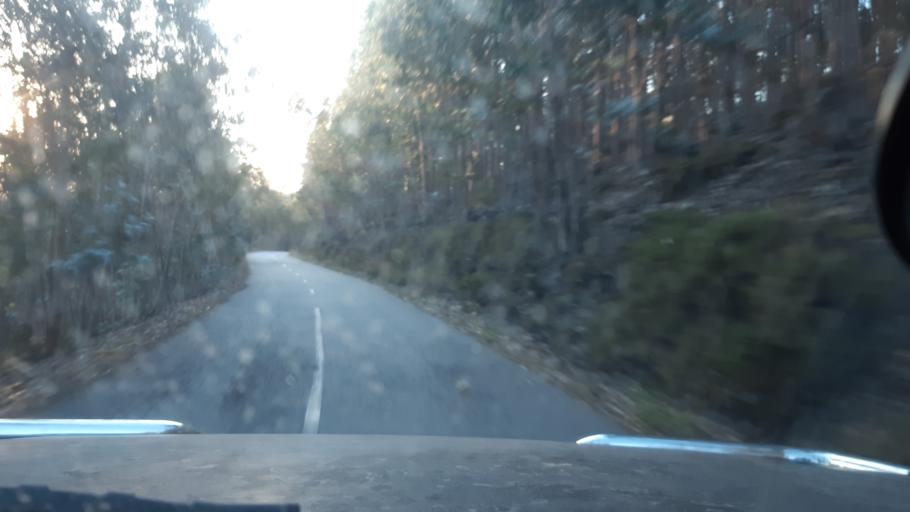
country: PT
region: Aveiro
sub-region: Agueda
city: Aguada de Cima
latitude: 40.5582
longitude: -8.2939
